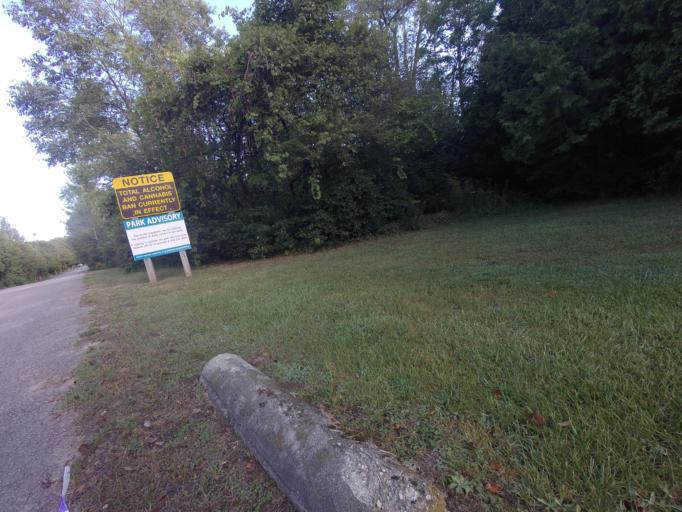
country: CA
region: Ontario
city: Waterloo
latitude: 43.6704
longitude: -80.4427
